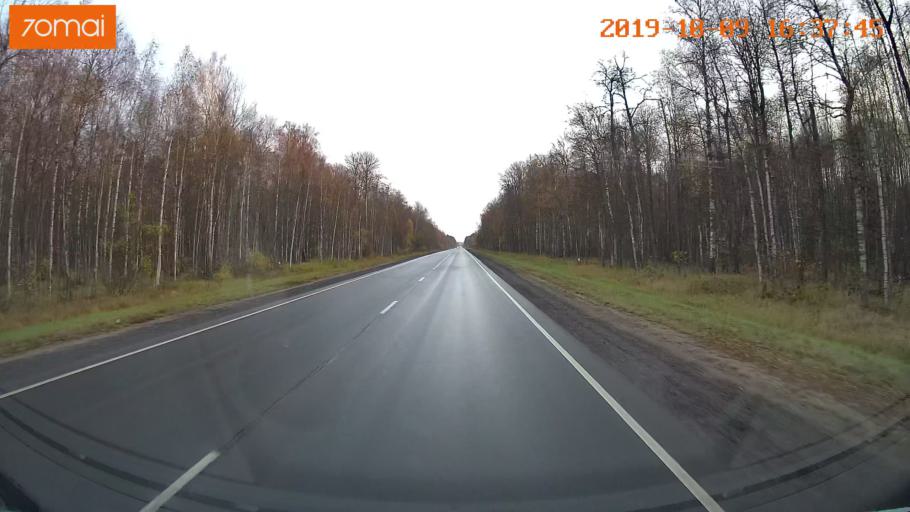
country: RU
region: Kostroma
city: Volgorechensk
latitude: 57.5222
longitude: 41.0286
